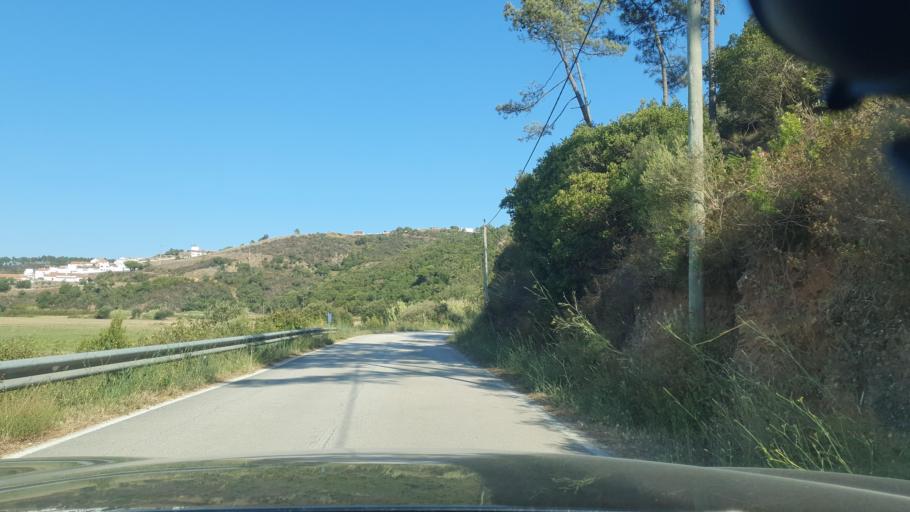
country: PT
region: Beja
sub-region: Odemira
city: Sao Teotonio
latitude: 37.4320
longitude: -8.7801
